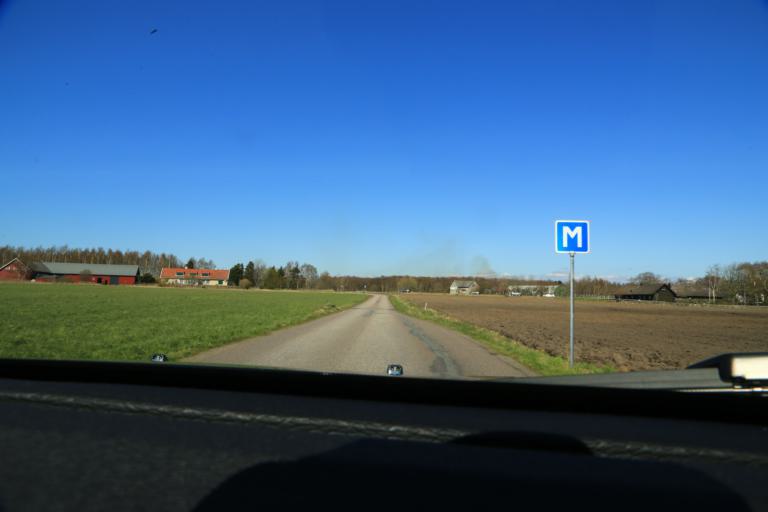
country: SE
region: Halland
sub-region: Varbergs Kommun
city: Traslovslage
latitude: 57.0464
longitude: 12.3088
